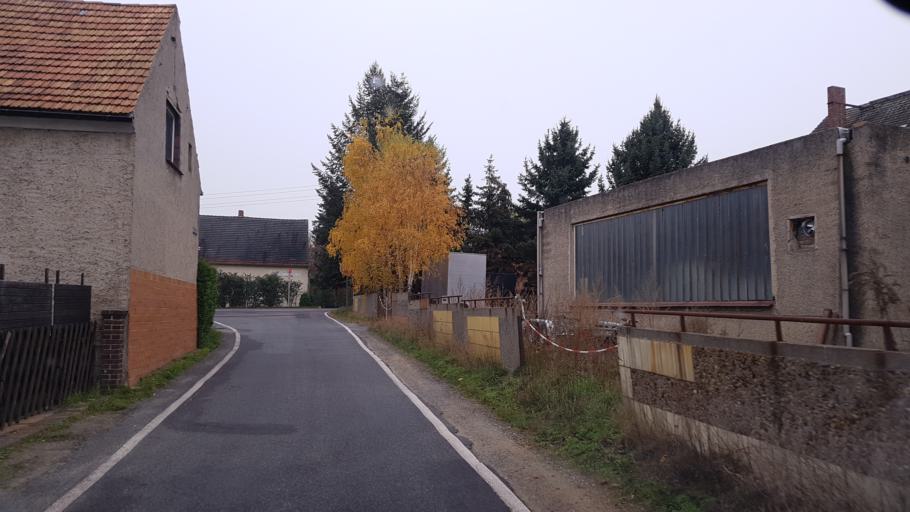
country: DE
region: Brandenburg
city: Crinitz
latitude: 51.7382
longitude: 13.7585
